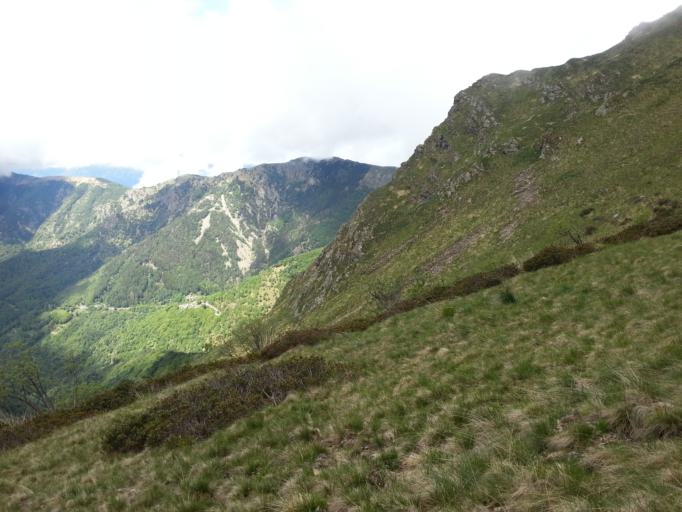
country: CH
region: Ticino
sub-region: Locarno District
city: Magadino
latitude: 46.0985
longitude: 8.8677
